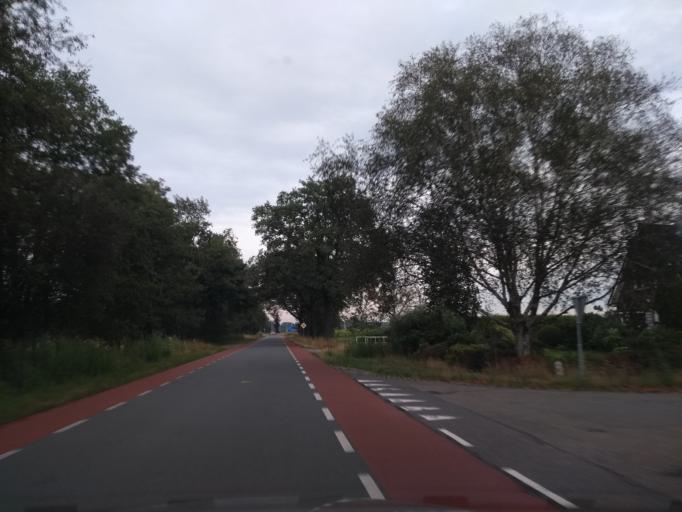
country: NL
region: Gelderland
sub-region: Oude IJsselstreek
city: Varsseveld
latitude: 51.9529
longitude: 6.4820
